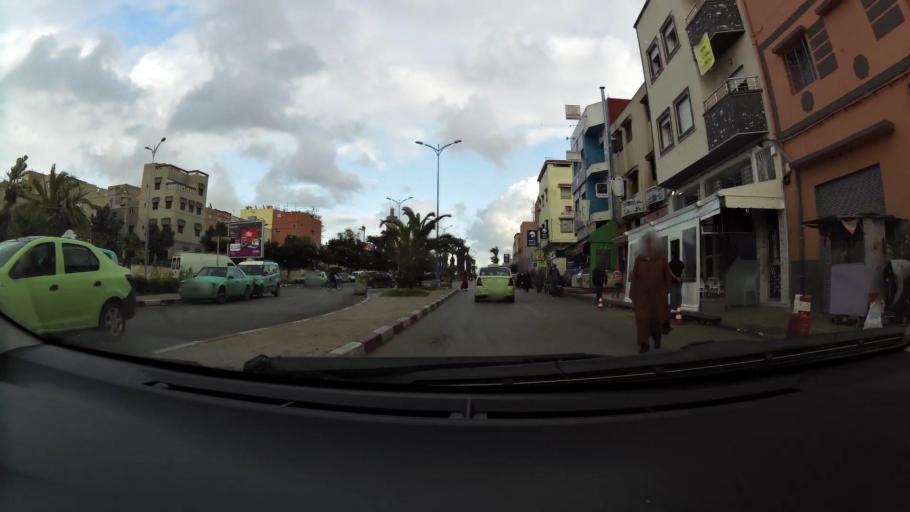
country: MA
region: Grand Casablanca
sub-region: Mohammedia
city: Mohammedia
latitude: 33.6882
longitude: -7.3922
